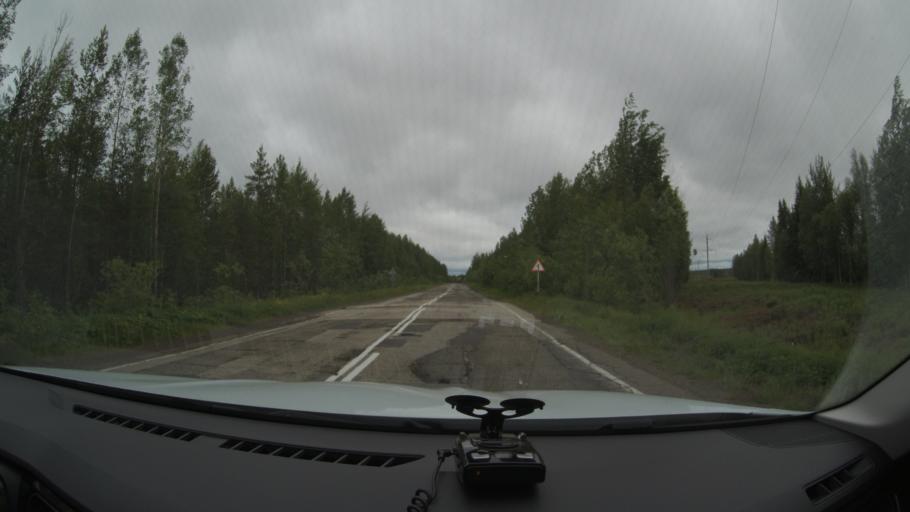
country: RU
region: Komi Republic
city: Nizhniy Odes
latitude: 63.6215
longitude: 54.6098
